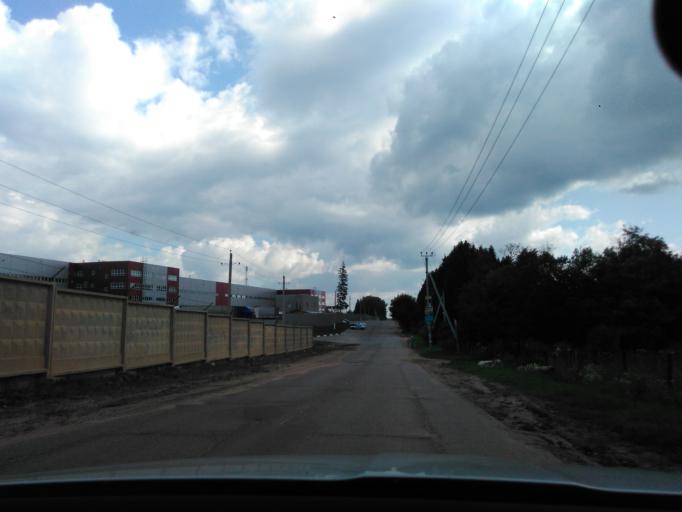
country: RU
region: Moskovskaya
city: Radumlya
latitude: 56.1266
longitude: 37.2057
